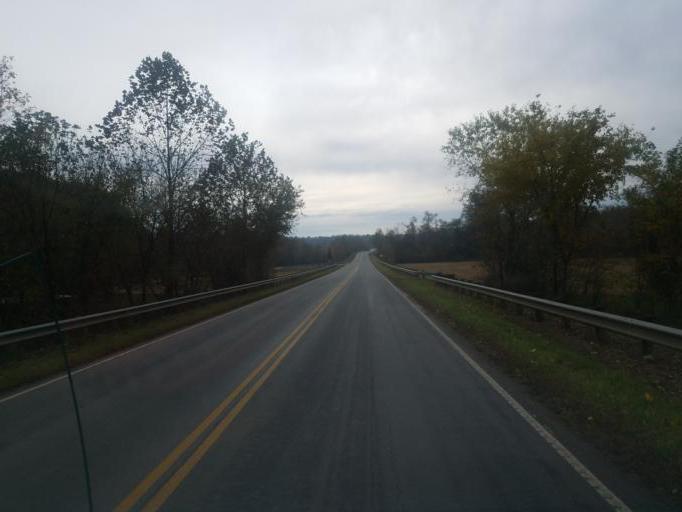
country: US
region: Ohio
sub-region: Washington County
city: Beverly
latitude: 39.5477
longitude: -81.6466
